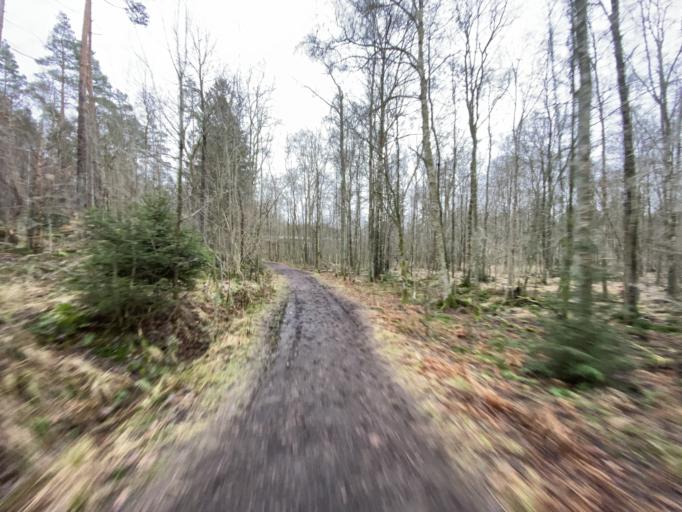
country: SE
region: Vaestra Goetaland
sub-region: Molndal
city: Moelndal
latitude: 57.7064
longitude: 12.0359
